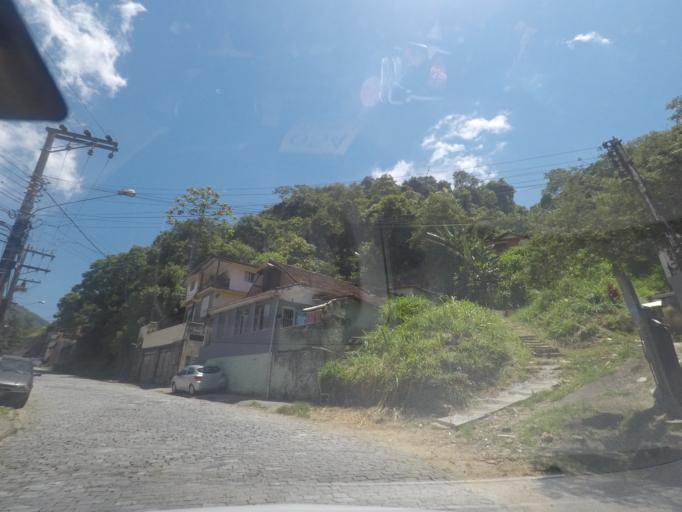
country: BR
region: Rio de Janeiro
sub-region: Petropolis
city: Petropolis
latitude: -22.5326
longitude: -43.1724
